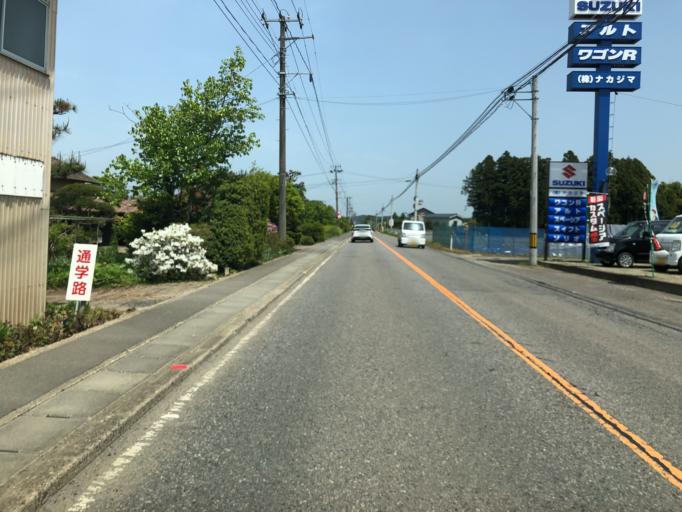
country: JP
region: Fukushima
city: Ishikawa
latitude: 37.1373
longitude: 140.3865
